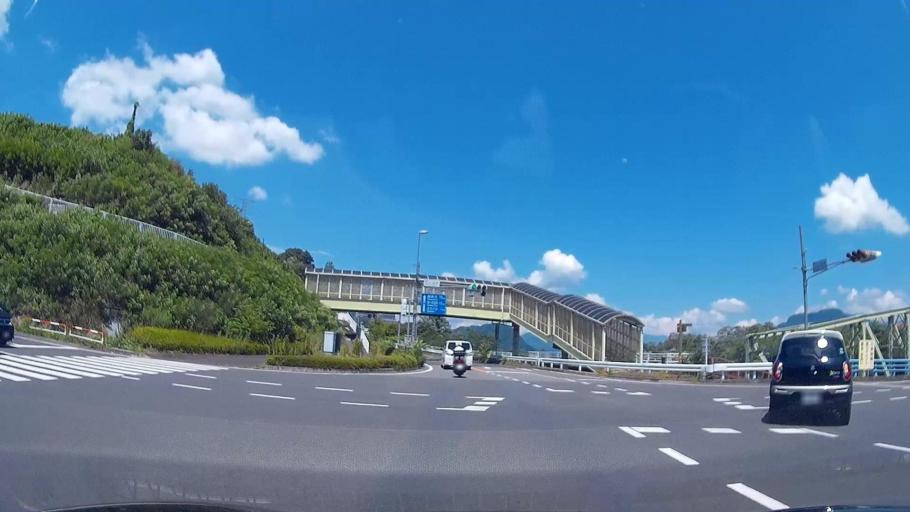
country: JP
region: Gunma
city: Numata
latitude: 36.6318
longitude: 139.0369
